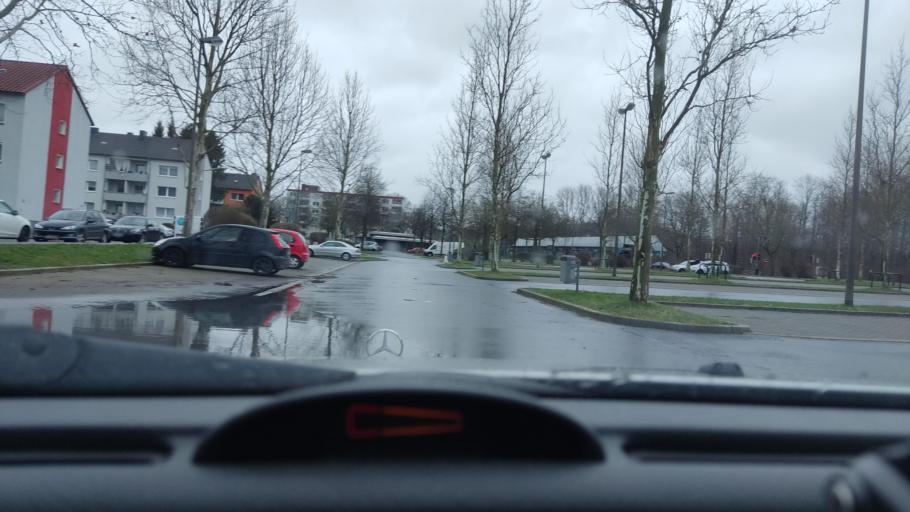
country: DE
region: North Rhine-Westphalia
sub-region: Regierungsbezirk Arnsberg
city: Dortmund
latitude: 51.5490
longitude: 7.4890
